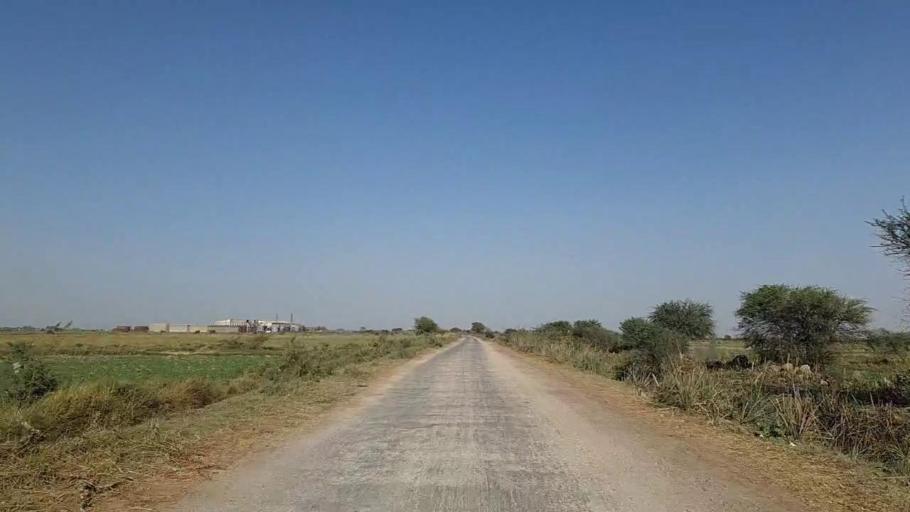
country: PK
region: Sindh
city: Chuhar Jamali
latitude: 24.5290
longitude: 68.1220
